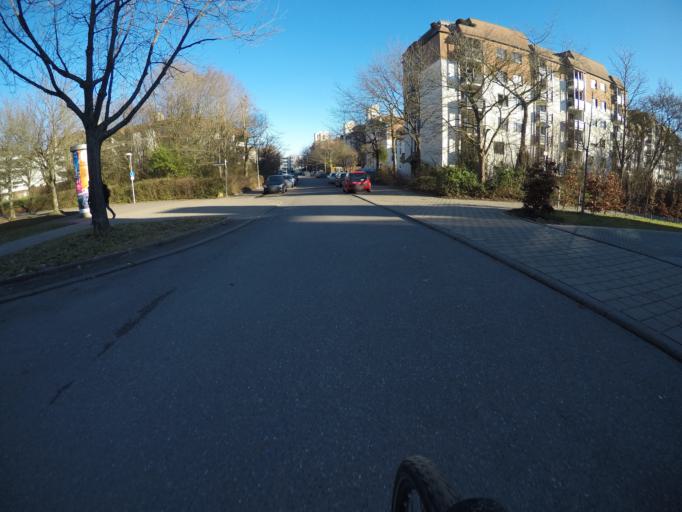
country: DE
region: Baden-Wuerttemberg
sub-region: Regierungsbezirk Stuttgart
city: Ostfildern
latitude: 48.7380
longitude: 9.2274
